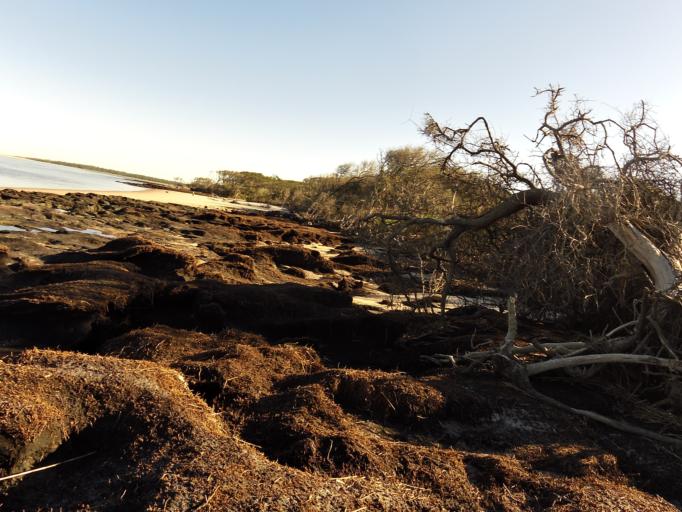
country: US
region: Florida
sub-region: Duval County
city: Atlantic Beach
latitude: 30.4979
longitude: -81.4418
